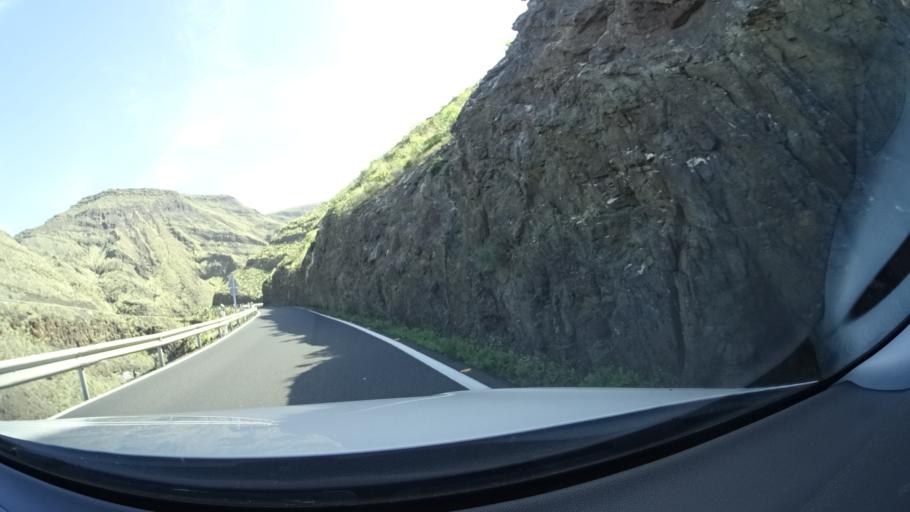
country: ES
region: Canary Islands
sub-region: Provincia de Las Palmas
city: Agaete
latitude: 28.0833
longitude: -15.7058
